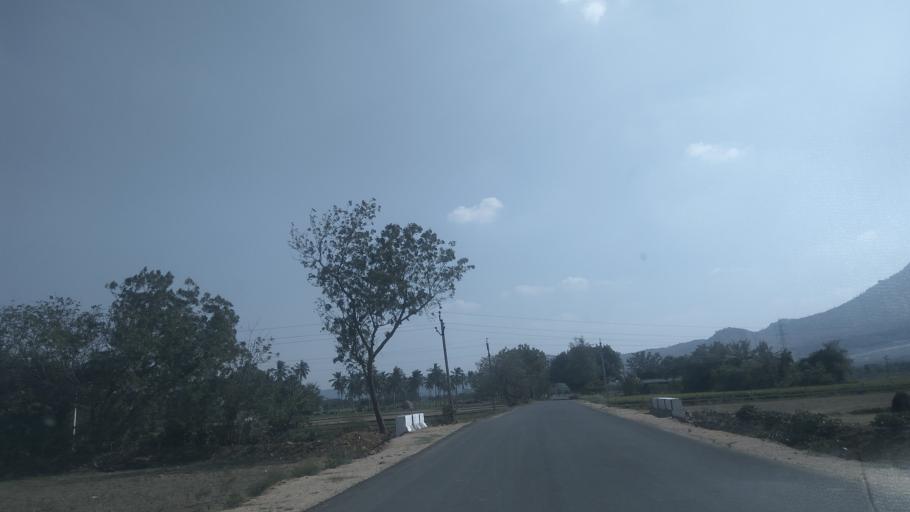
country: IN
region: Andhra Pradesh
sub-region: Chittoor
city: Renigunta
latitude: 13.5540
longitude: 79.4827
